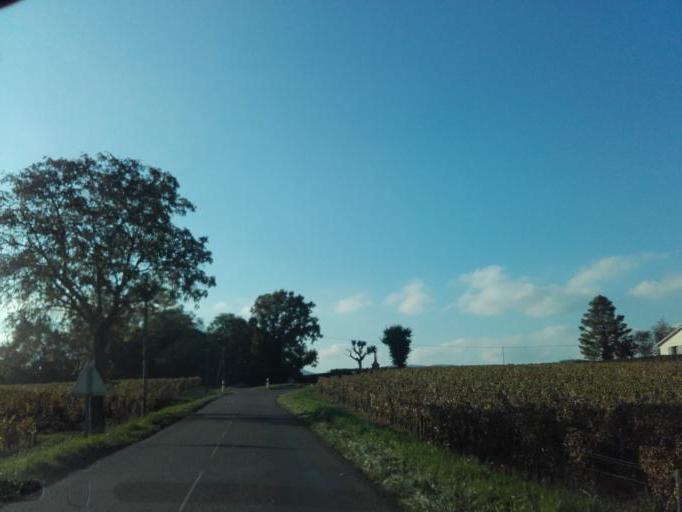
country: FR
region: Bourgogne
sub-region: Departement de Saone-et-Loire
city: Creches-sur-Saone
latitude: 46.2495
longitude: 4.7654
